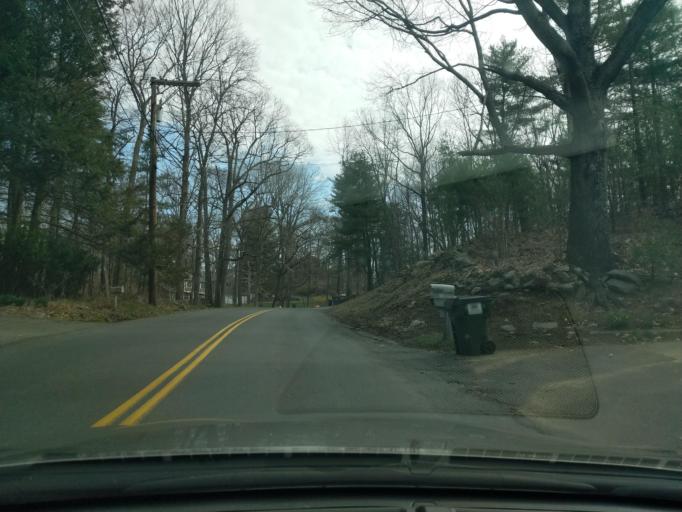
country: US
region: Connecticut
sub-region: Fairfield County
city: Newtown
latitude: 41.3405
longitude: -73.2432
